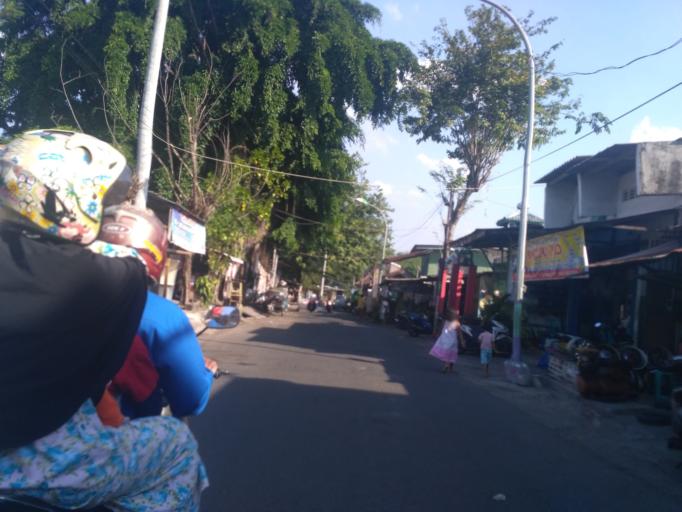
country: ID
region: Central Java
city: Semarang
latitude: -6.9982
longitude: 110.4382
